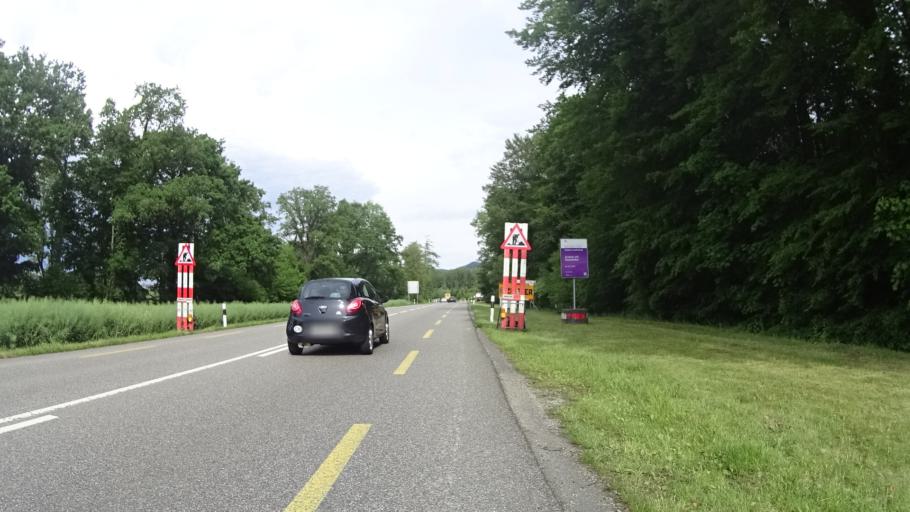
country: DE
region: Baden-Wuerttemberg
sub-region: Freiburg Region
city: Murg
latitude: 47.5492
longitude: 8.0184
